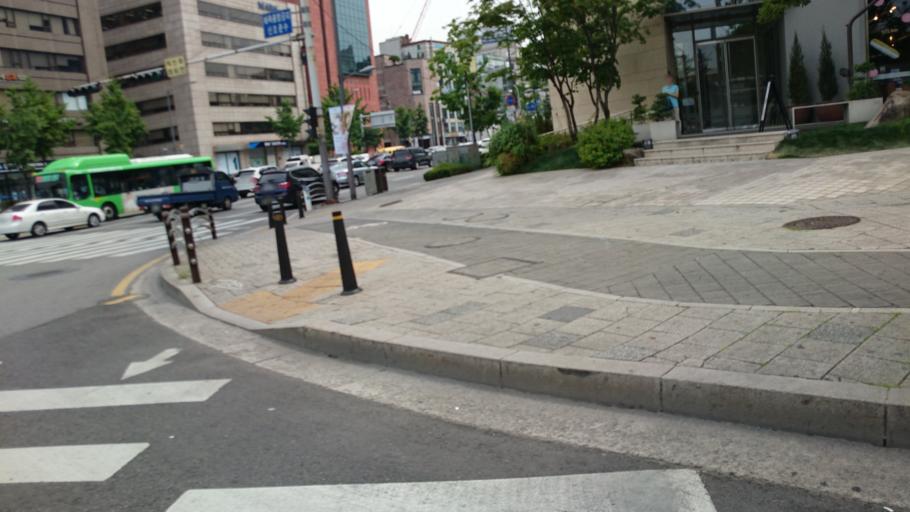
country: KR
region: Seoul
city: Seoul
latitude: 37.5291
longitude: 127.0335
